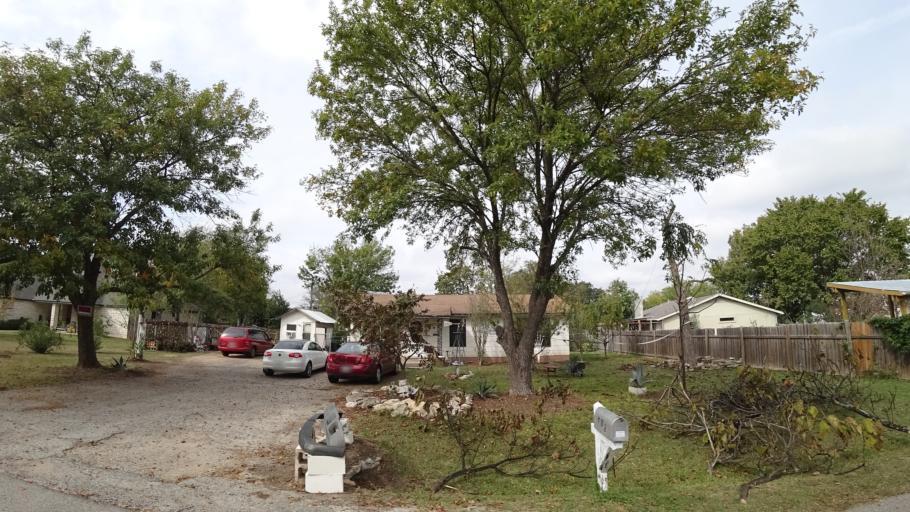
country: US
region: Texas
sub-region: Williamson County
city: Round Rock
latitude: 30.4961
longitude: -97.6880
